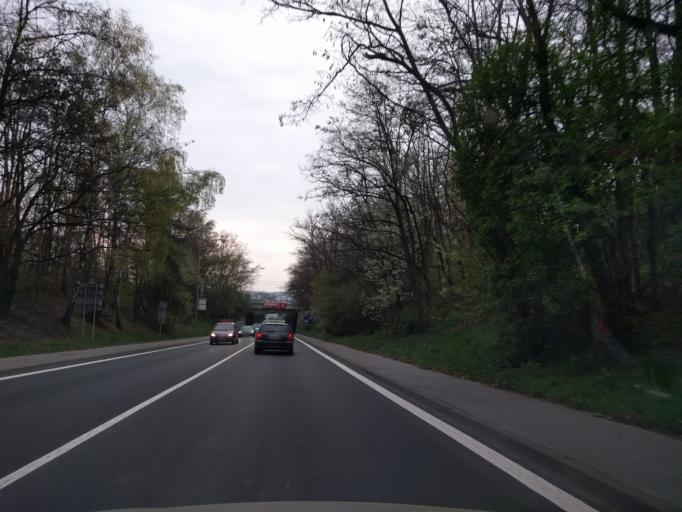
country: CZ
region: Central Bohemia
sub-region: Okres Praha-Vychod
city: Ricany
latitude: 50.0005
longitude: 14.6611
